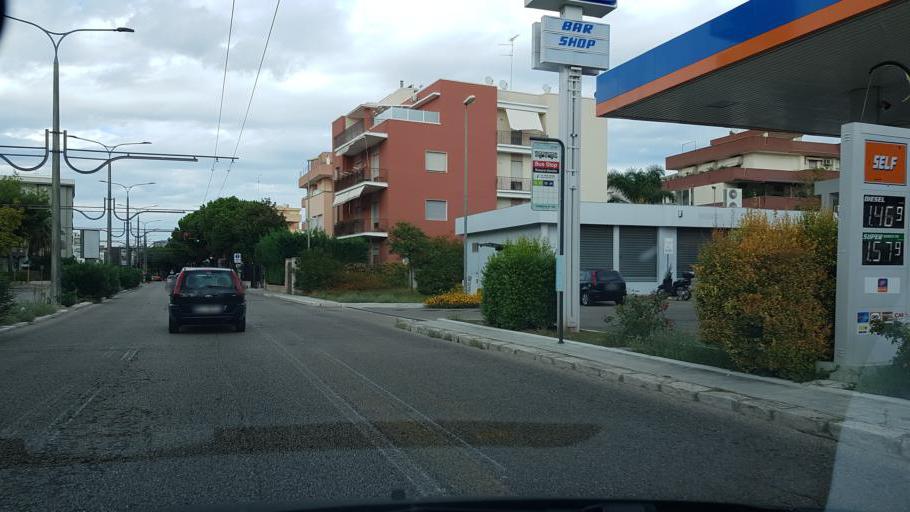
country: IT
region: Apulia
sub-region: Provincia di Lecce
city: Lecce
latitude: 40.3497
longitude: 18.1857
